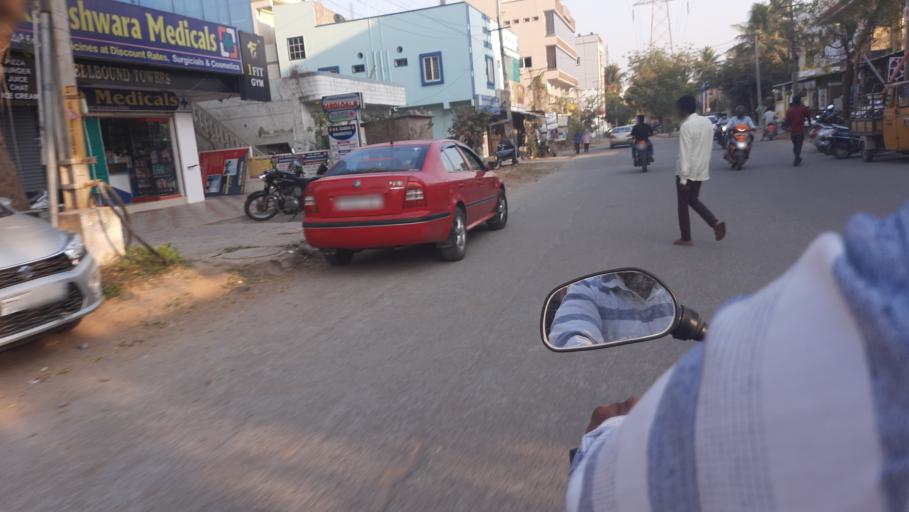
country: IN
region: Telangana
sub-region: Rangareddi
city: Secunderabad
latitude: 17.4959
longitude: 78.5440
